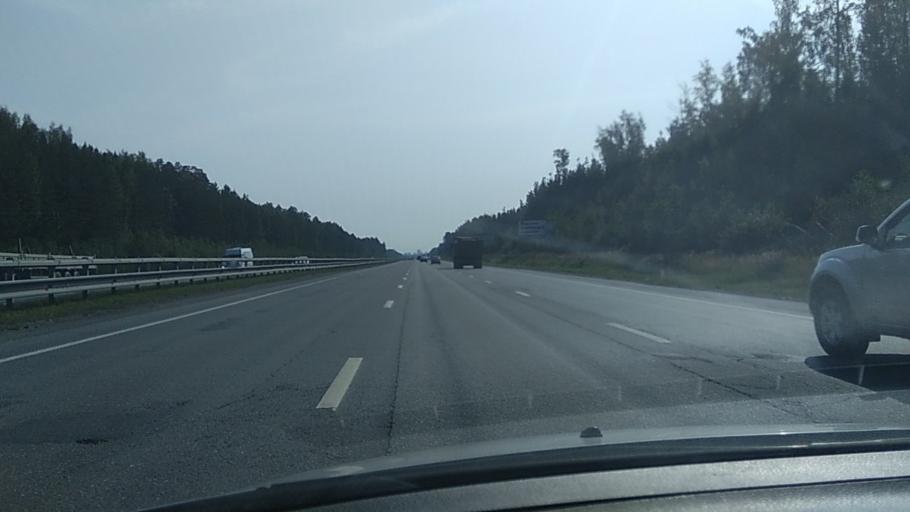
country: RU
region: Sverdlovsk
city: Shuvakish
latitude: 56.9582
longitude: 60.5154
